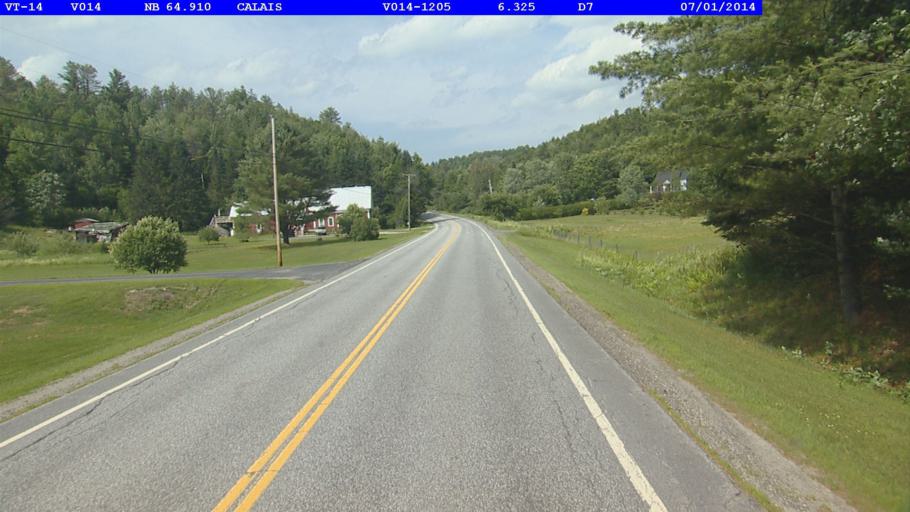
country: US
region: Vermont
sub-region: Caledonia County
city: Hardwick
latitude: 44.3881
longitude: -72.4158
